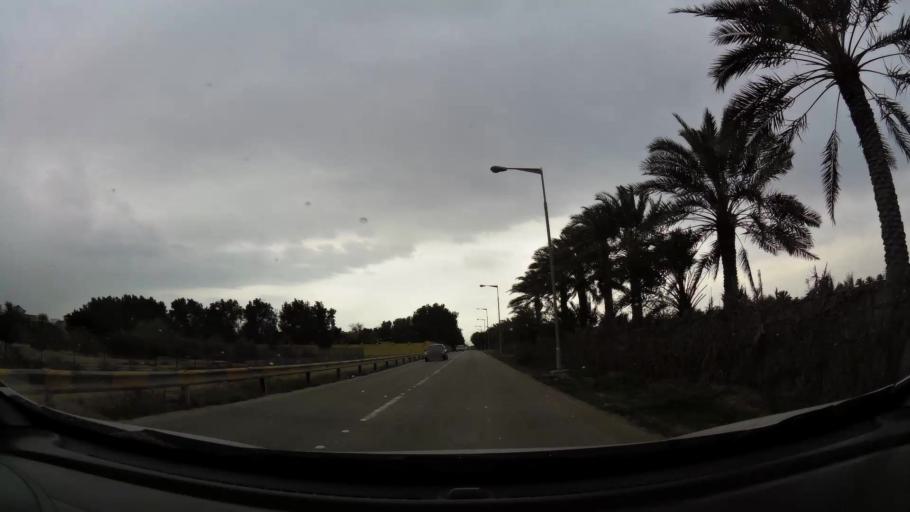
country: BH
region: Central Governorate
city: Madinat Hamad
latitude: 26.1548
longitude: 50.4626
